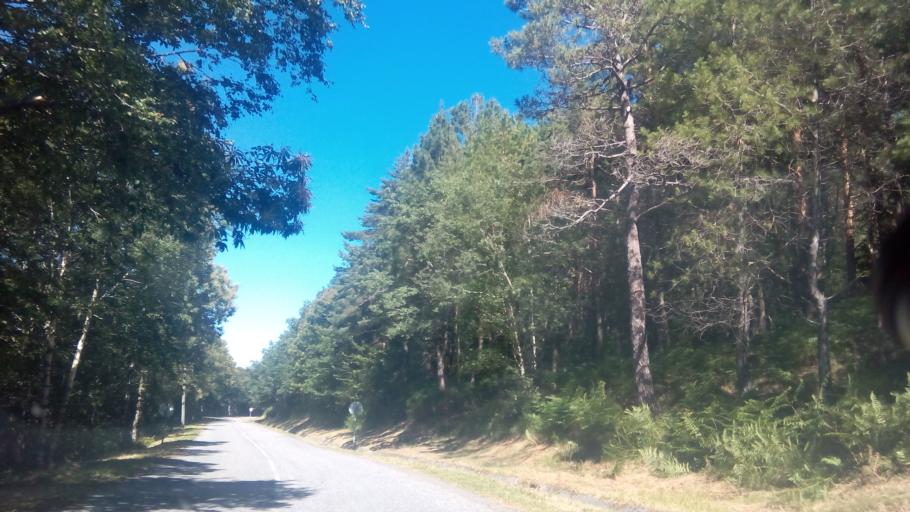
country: PT
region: Vila Real
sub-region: Mesao Frio
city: Mesao Frio
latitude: 41.2758
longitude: -7.8996
